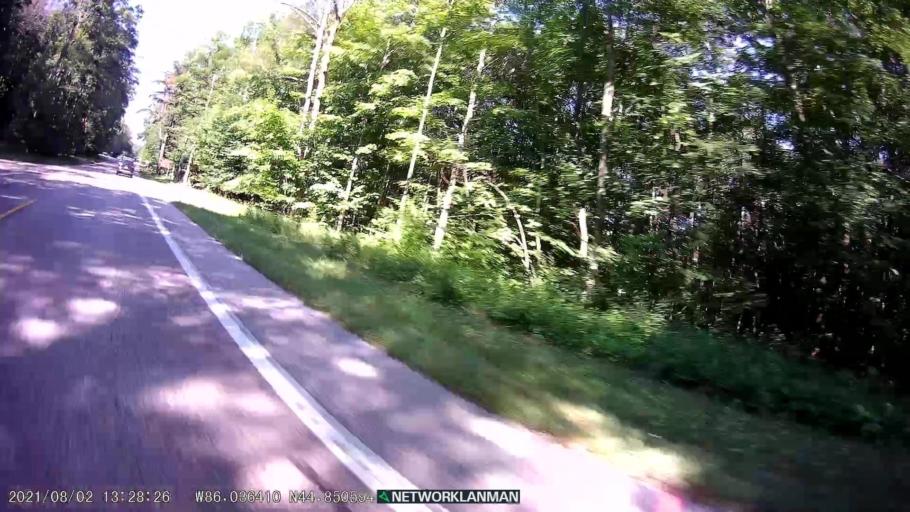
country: US
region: Michigan
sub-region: Benzie County
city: Beulah
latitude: 44.8506
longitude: -86.0365
